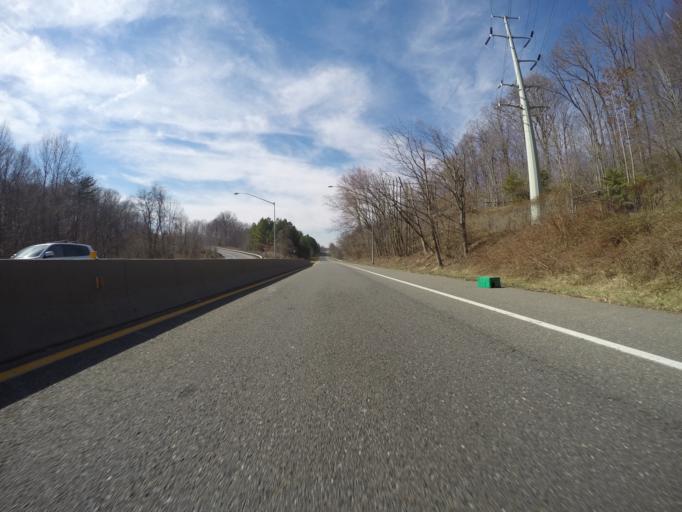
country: US
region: Maryland
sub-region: Anne Arundel County
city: Crownsville
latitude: 39.0427
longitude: -76.6100
